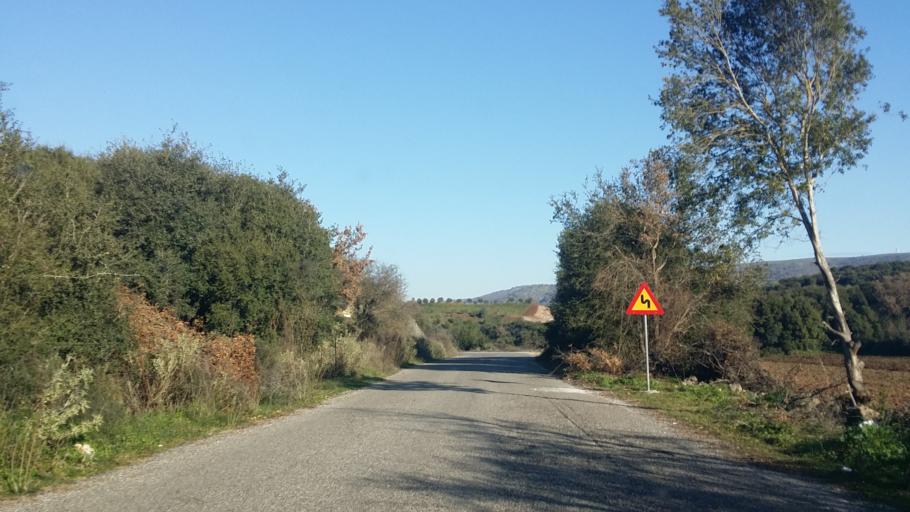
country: GR
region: West Greece
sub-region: Nomos Aitolias kai Akarnanias
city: Katouna
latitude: 38.7698
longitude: 21.1339
